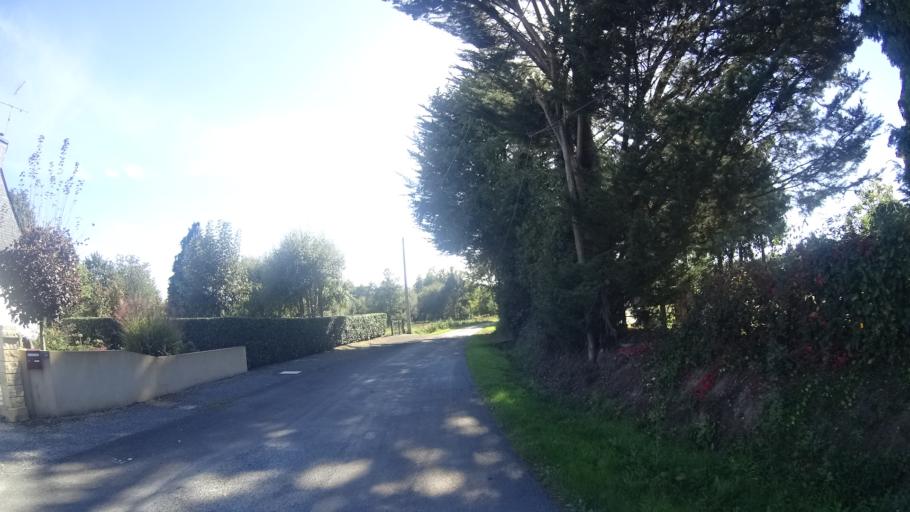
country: FR
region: Brittany
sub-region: Departement du Morbihan
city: Peillac
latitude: 47.7341
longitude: -2.1984
